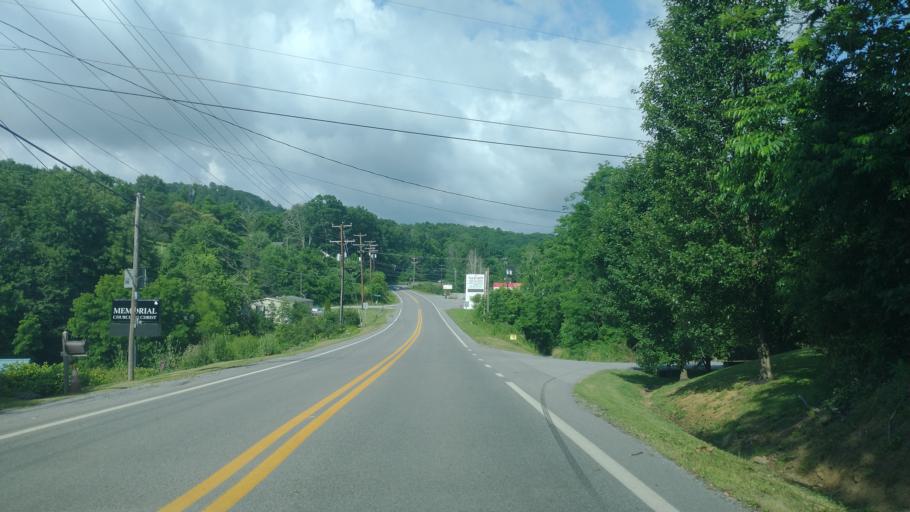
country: US
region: West Virginia
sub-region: Mercer County
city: Princeton
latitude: 37.3619
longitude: -81.1261
